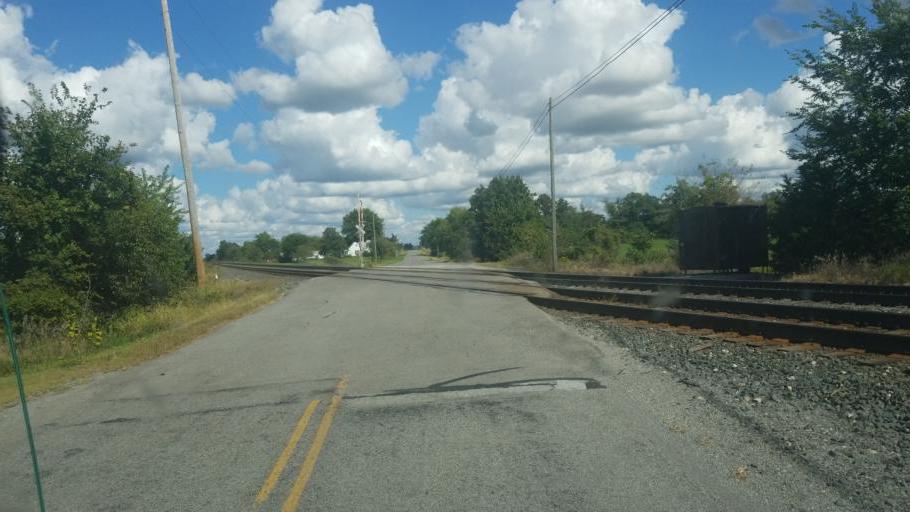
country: US
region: Ohio
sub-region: Logan County
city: Northwood
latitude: 40.5024
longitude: -83.6159
